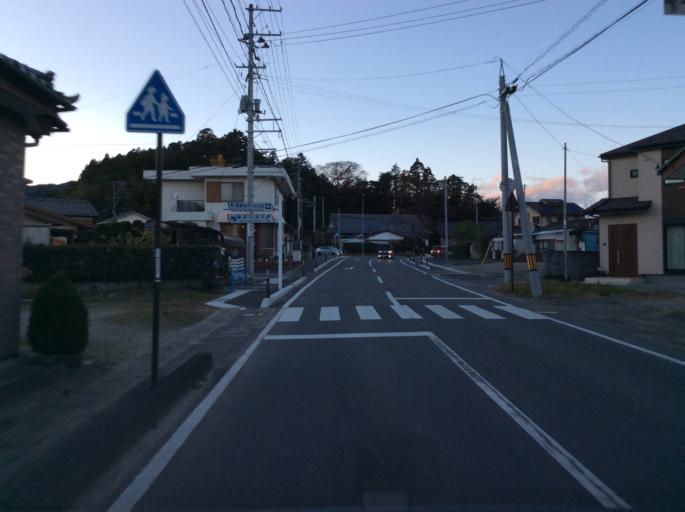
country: JP
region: Fukushima
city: Iwaki
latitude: 37.1263
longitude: 140.8548
